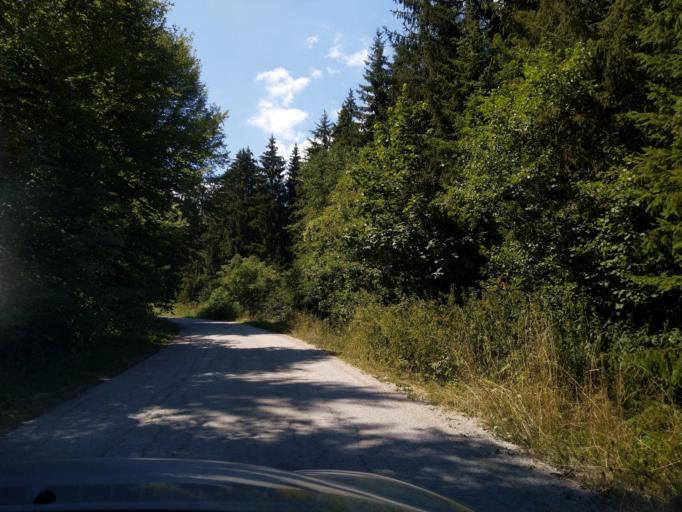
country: RS
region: Central Serbia
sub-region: Zlatiborski Okrug
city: Nova Varos
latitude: 43.4790
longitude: 19.9699
